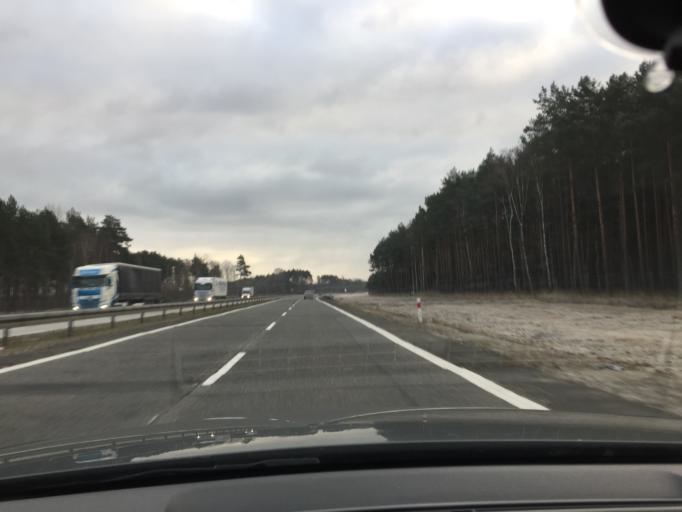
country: PL
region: Lubusz
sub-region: Powiat zarski
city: Lipinki Luzyckie
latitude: 51.6124
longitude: 14.9533
